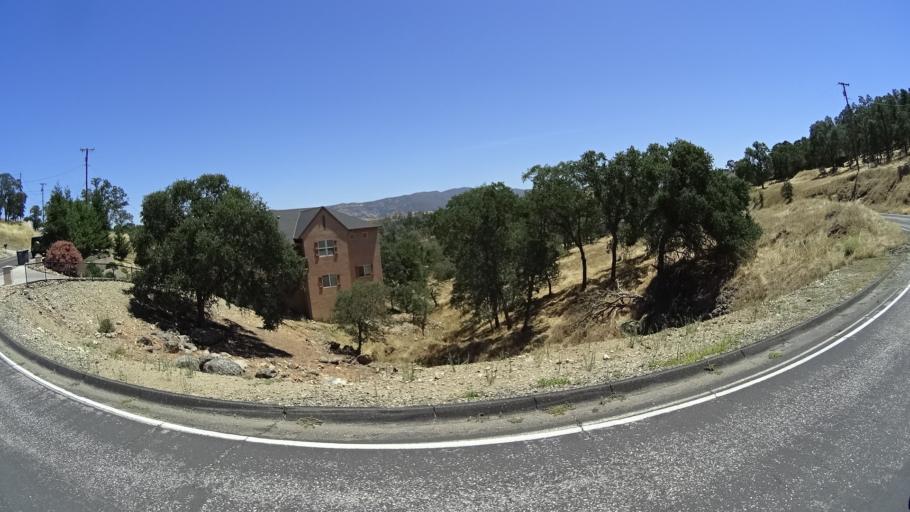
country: US
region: California
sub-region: Calaveras County
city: Rancho Calaveras
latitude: 38.1504
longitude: -120.8415
